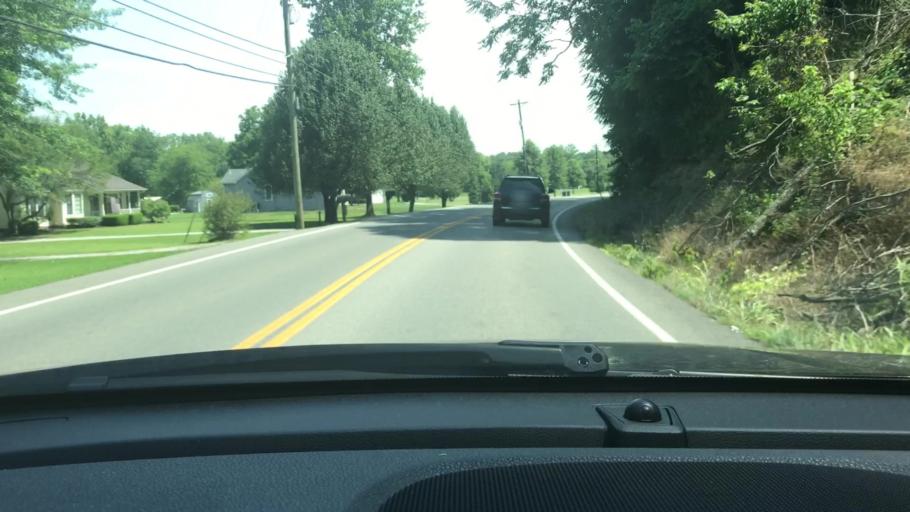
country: US
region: Tennessee
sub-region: Sumner County
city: Shackle Island
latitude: 36.3643
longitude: -86.6120
